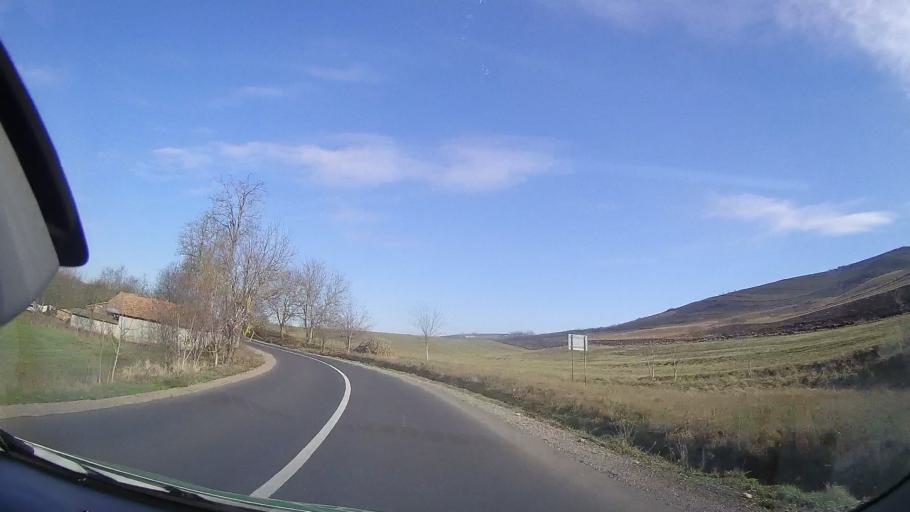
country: RO
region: Mures
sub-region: Comuna Zau De Campie
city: Zau de Campie
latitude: 46.5885
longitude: 24.1035
